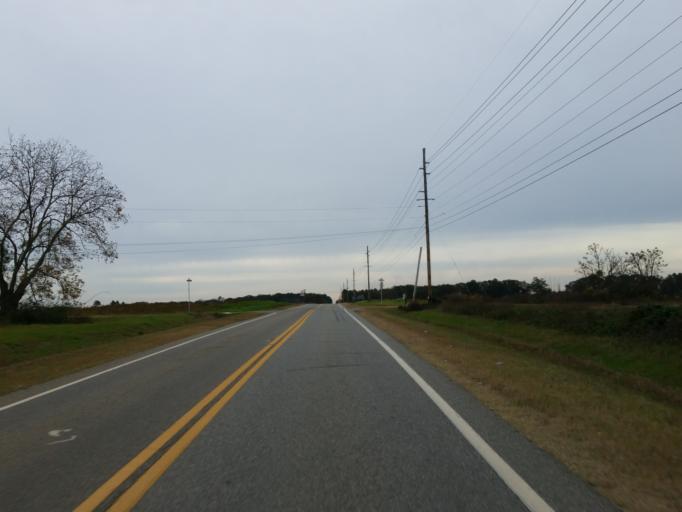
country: US
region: Georgia
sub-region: Crisp County
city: Cordele
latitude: 31.9129
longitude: -83.7083
